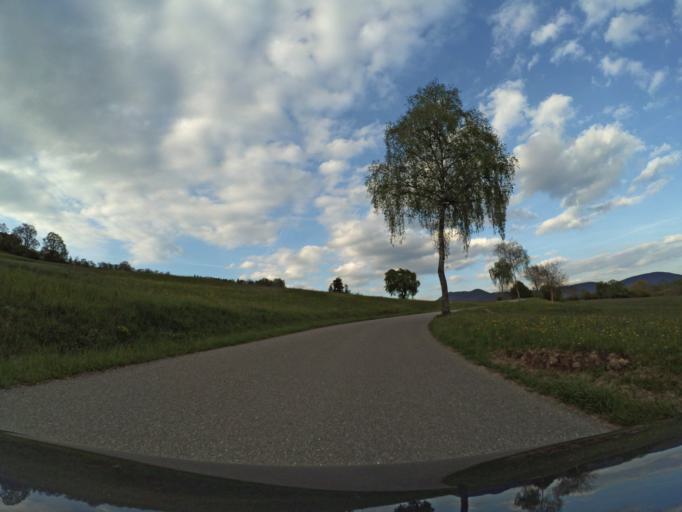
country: CH
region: Schaffhausen
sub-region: Bezirk Unterklettgau
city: Hallau
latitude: 47.7176
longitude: 8.4775
